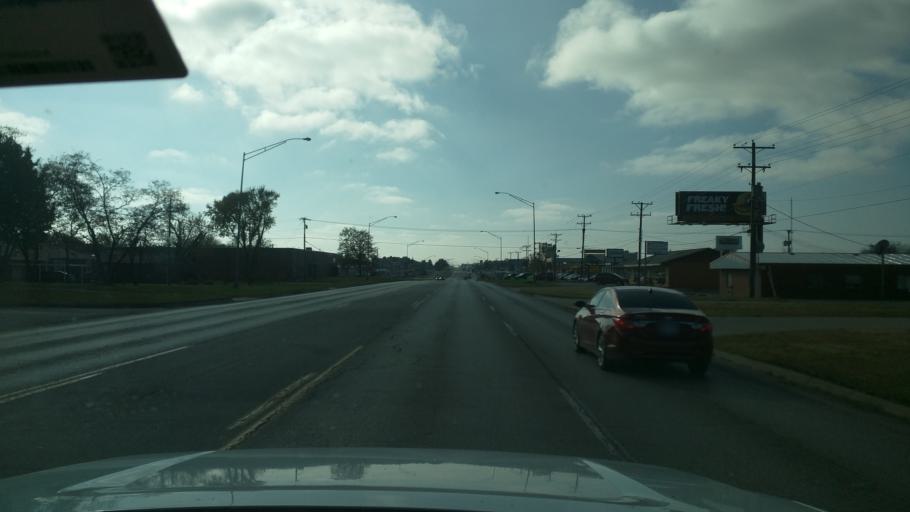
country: US
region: Oklahoma
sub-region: Washington County
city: Dewey
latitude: 36.7636
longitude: -95.9355
